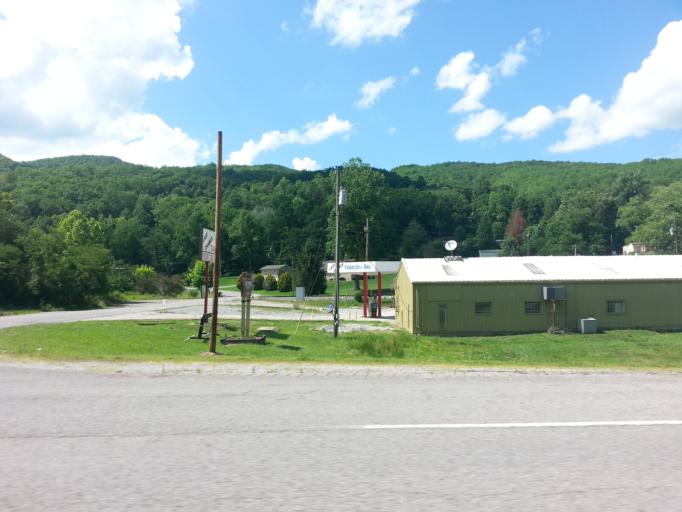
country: US
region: Kentucky
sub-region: Harlan County
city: Harlan
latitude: 36.9144
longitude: -83.1921
